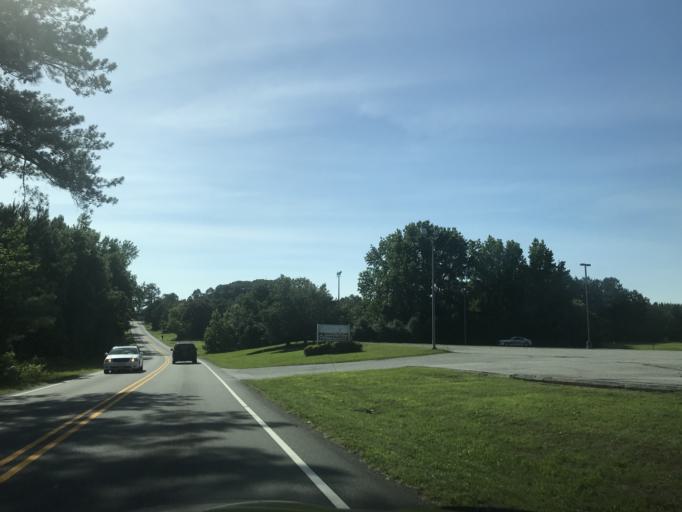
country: US
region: North Carolina
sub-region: Wake County
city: Garner
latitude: 35.6615
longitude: -78.5476
